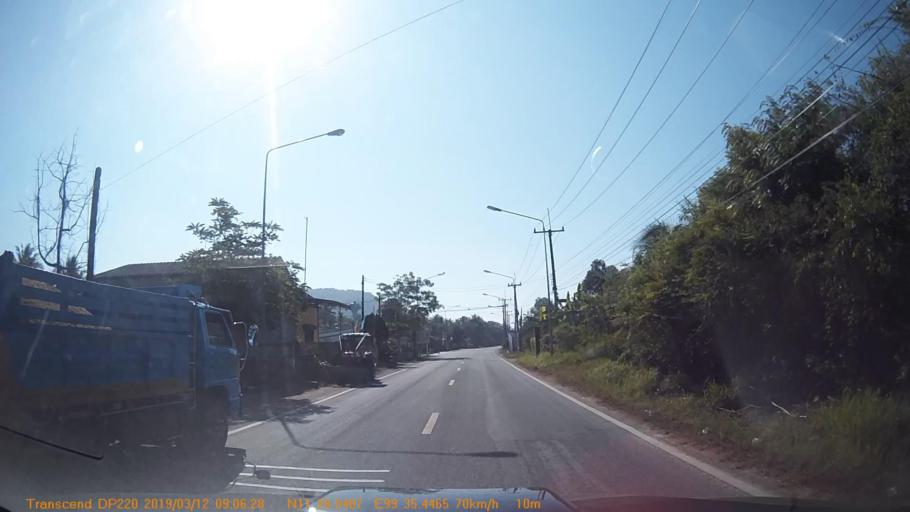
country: TH
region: Prachuap Khiri Khan
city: Thap Sakae
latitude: 11.4339
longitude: 99.5910
